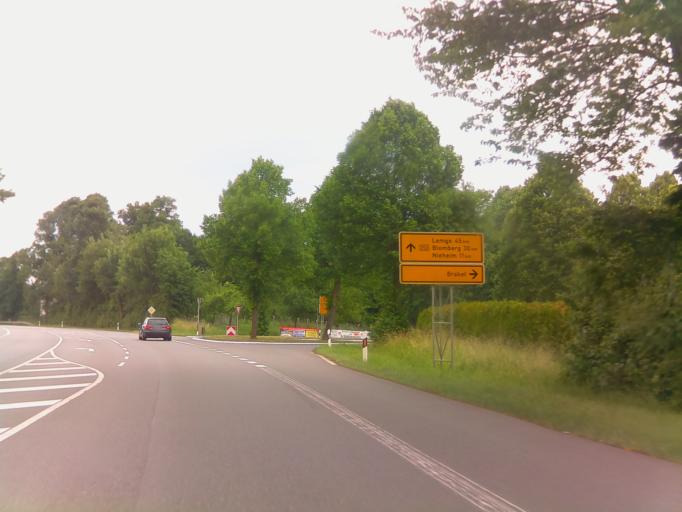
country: DE
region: North Rhine-Westphalia
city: Brakel
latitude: 51.7229
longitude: 9.1699
